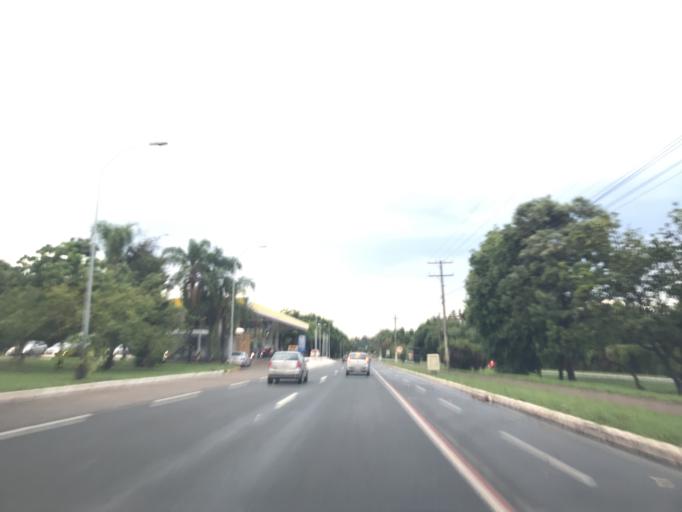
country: BR
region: Federal District
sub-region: Brasilia
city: Brasilia
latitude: -15.8444
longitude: -47.8715
